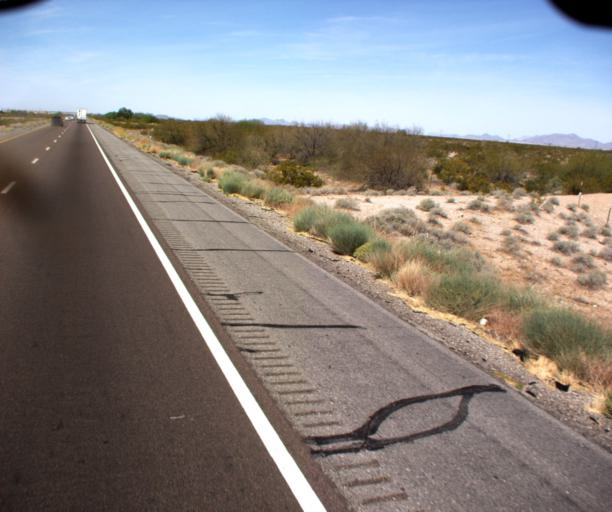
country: US
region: Arizona
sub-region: La Paz County
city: Salome
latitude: 33.5585
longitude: -113.2817
